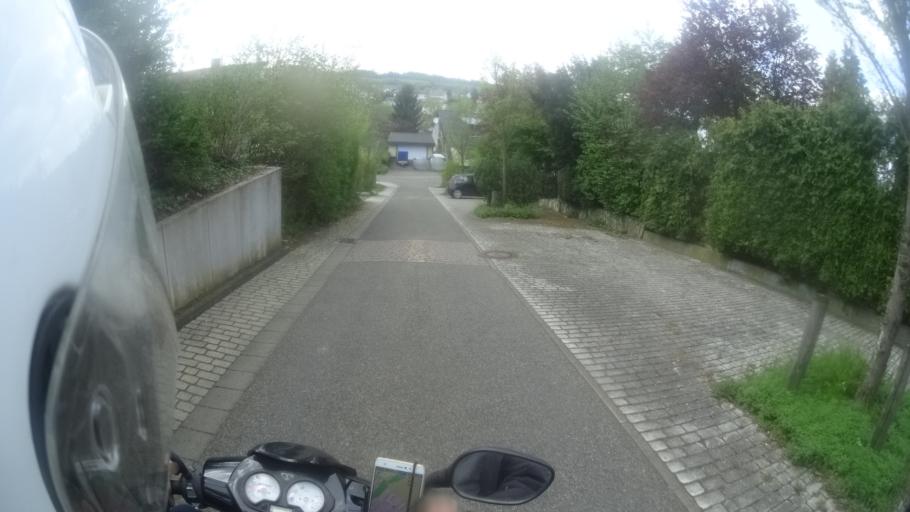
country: DE
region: Hesse
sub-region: Regierungsbezirk Darmstadt
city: Schlangenbad
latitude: 50.1026
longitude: 8.0786
